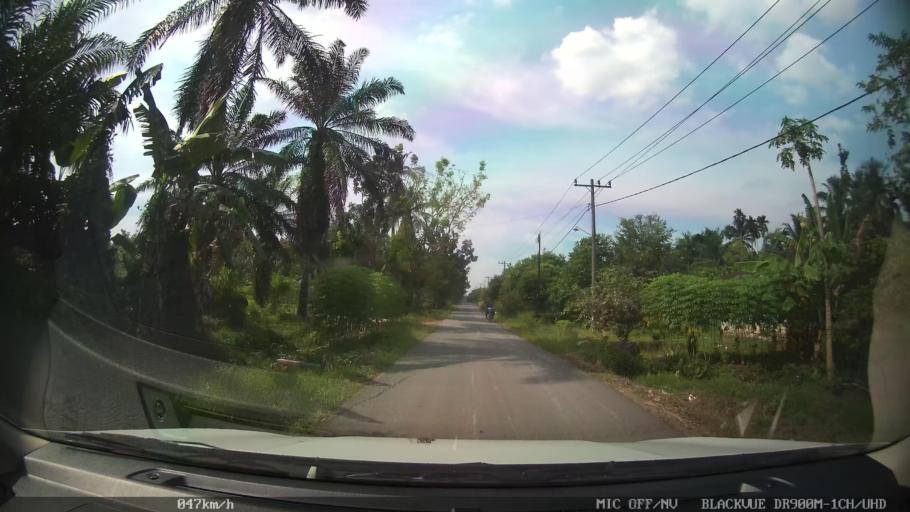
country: ID
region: North Sumatra
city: Binjai
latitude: 3.6463
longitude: 98.5177
